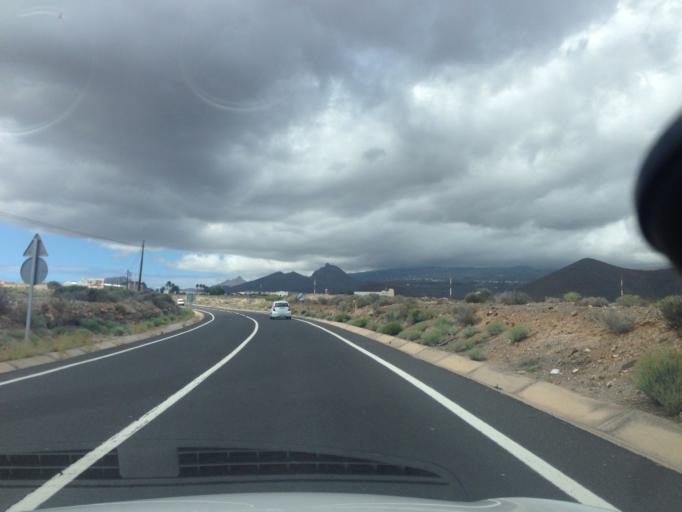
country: ES
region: Canary Islands
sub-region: Provincia de Santa Cruz de Tenerife
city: Las Rosas
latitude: 28.0436
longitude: -16.6064
